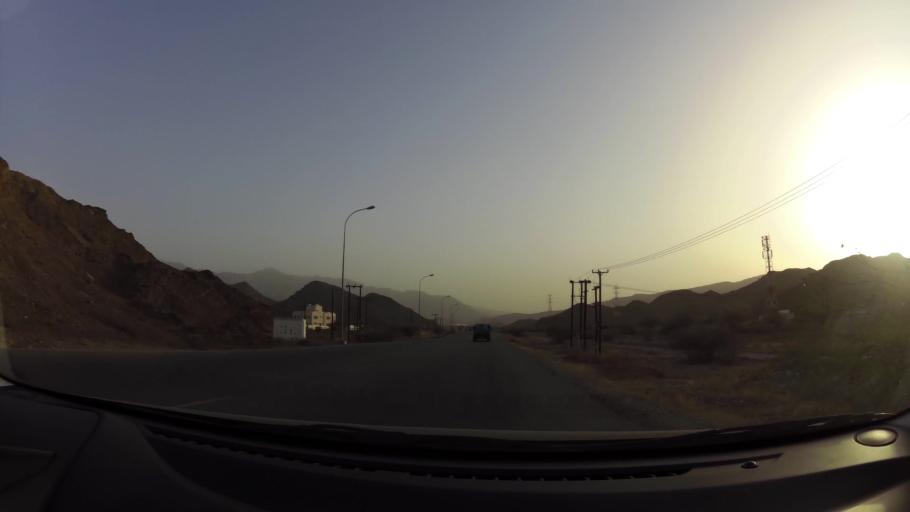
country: OM
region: Muhafazat Masqat
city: Bawshar
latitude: 23.5011
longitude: 58.3304
